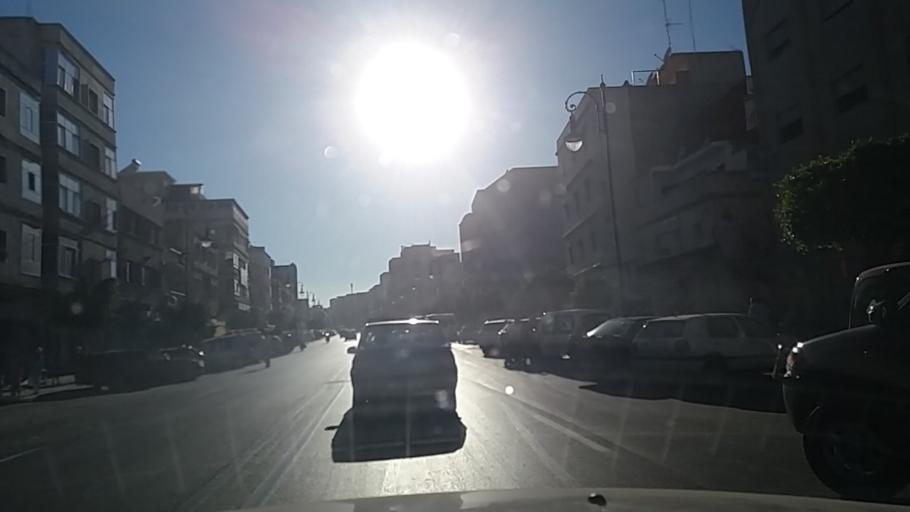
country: MA
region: Tanger-Tetouan
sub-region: Tanger-Assilah
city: Tangier
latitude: 35.7540
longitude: -5.8127
